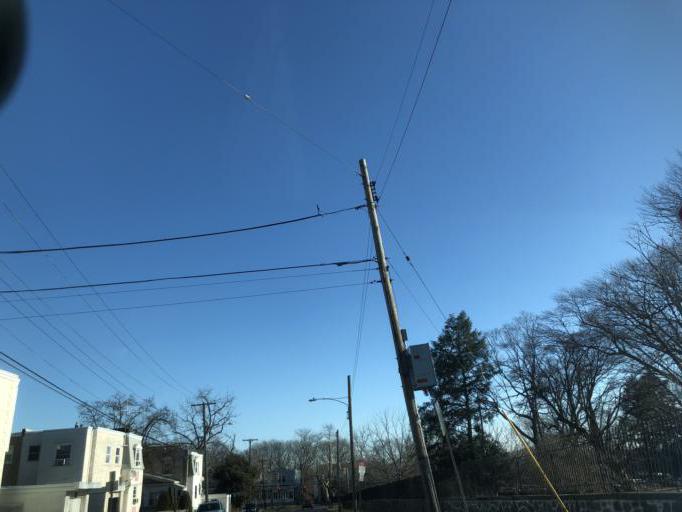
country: US
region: Pennsylvania
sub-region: Delaware County
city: Millbourne
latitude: 39.9570
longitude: -75.2537
